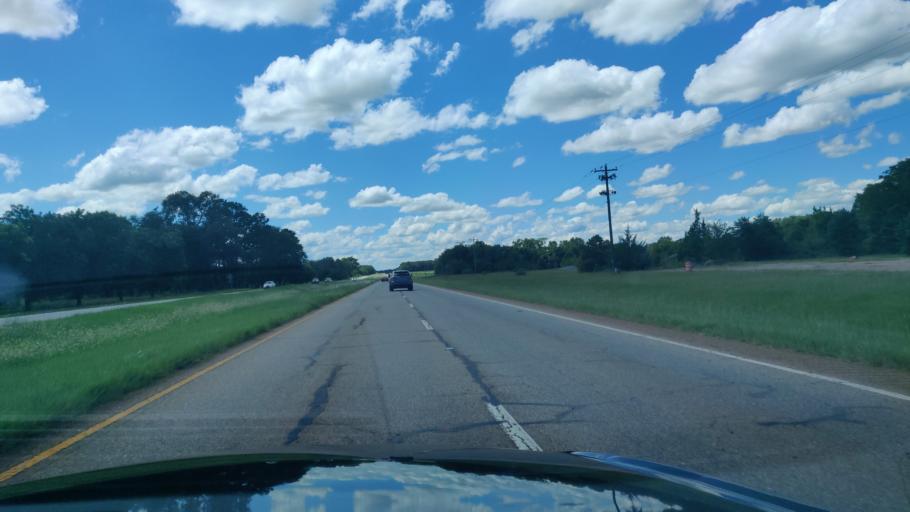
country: US
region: Georgia
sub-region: Webster County
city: Preston
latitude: 31.9504
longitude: -84.5796
